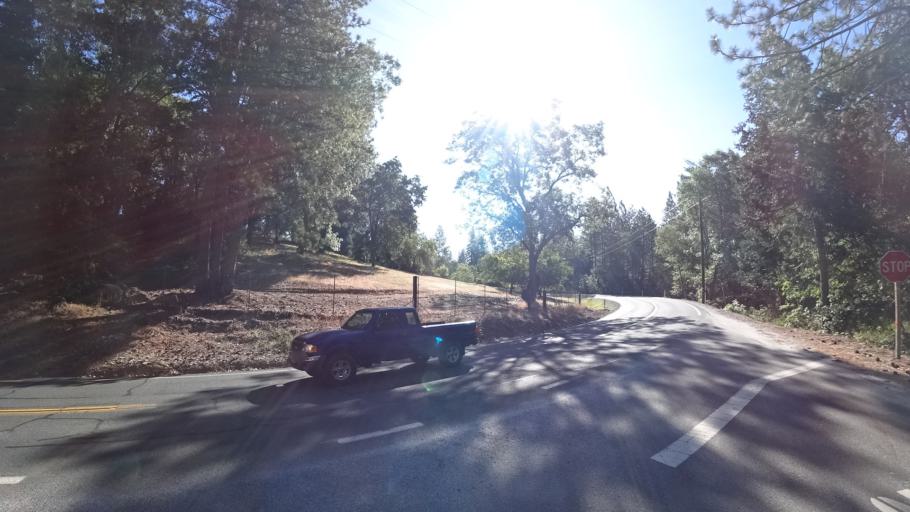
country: US
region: California
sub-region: Amador County
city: Pioneer
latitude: 38.4100
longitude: -120.5556
